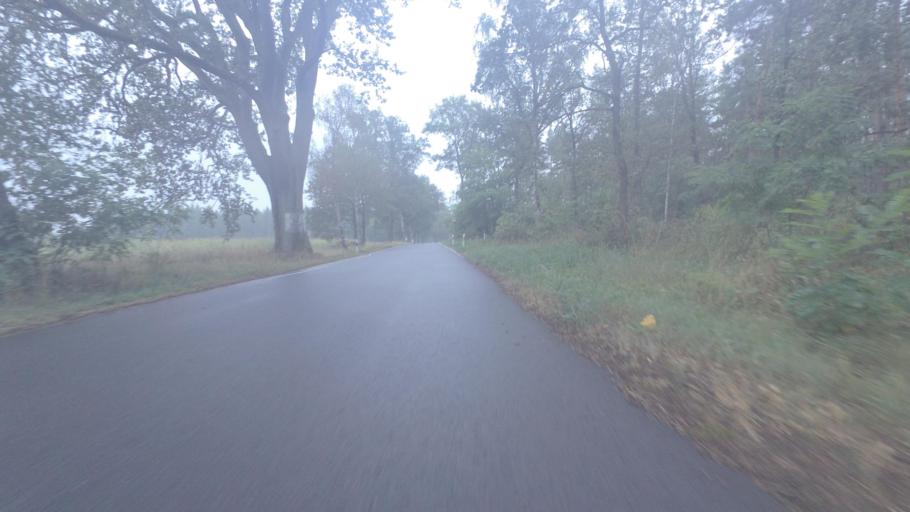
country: DE
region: Brandenburg
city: Heiligengrabe
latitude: 53.1603
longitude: 12.3463
